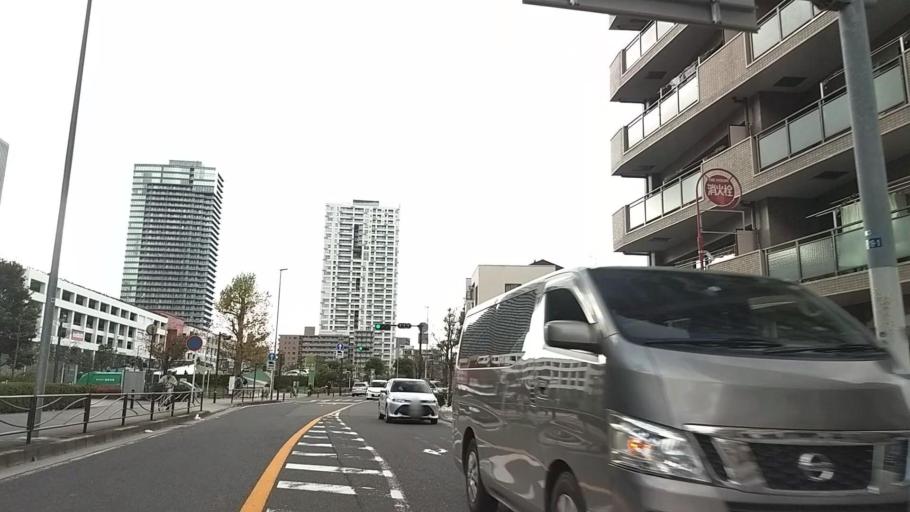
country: JP
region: Kanagawa
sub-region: Kawasaki-shi
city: Kawasaki
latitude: 35.5342
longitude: 139.6982
